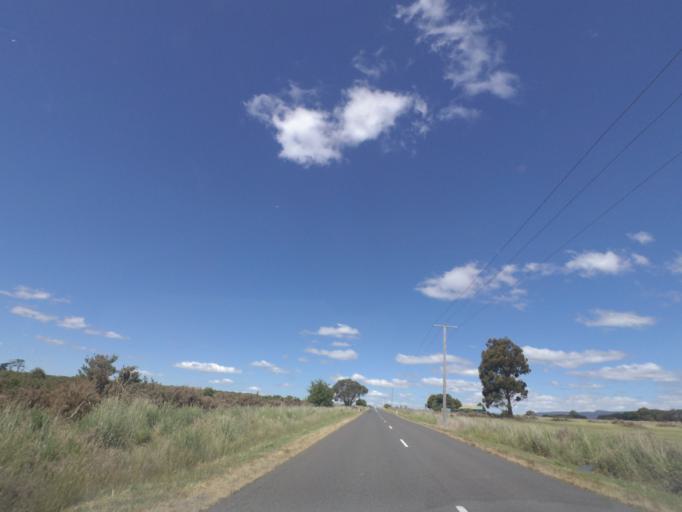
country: AU
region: Victoria
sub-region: Mount Alexander
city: Castlemaine
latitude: -37.2894
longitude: 144.4729
